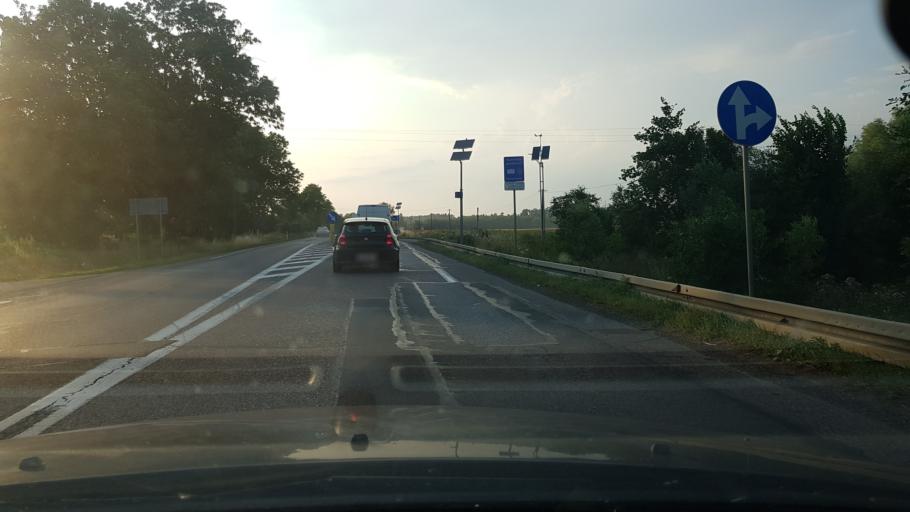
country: PL
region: Masovian Voivodeship
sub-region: Powiat plonski
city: Baboszewo
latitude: 52.7038
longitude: 20.3358
